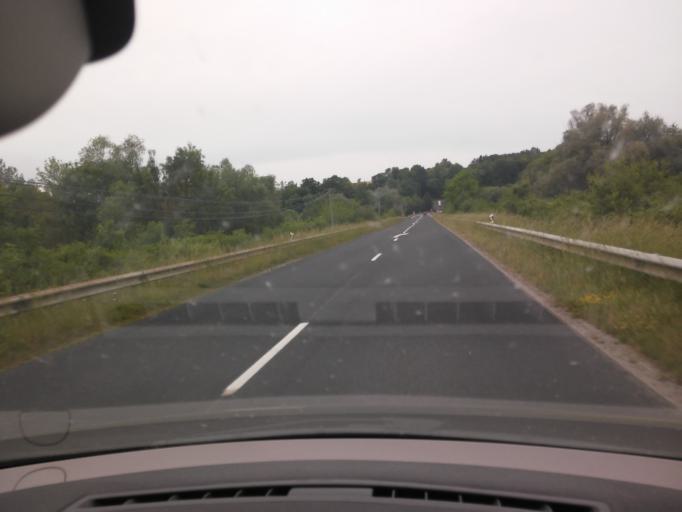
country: FR
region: Lorraine
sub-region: Departement de la Meuse
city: Saint-Mihiel
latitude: 48.8660
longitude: 5.5194
